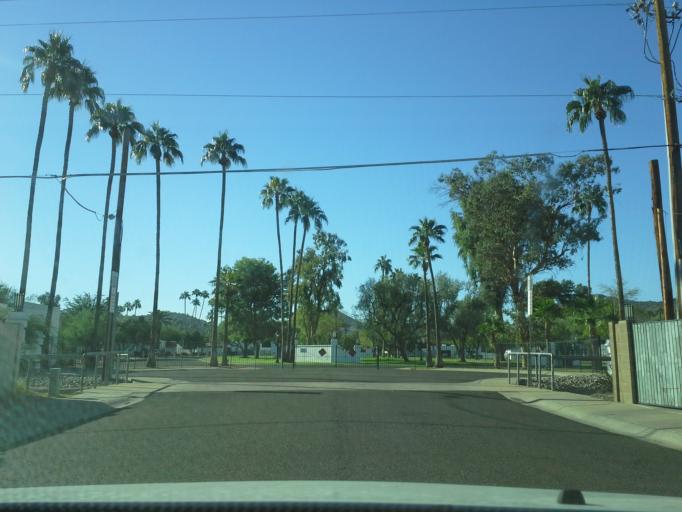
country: US
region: Arizona
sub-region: Maricopa County
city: Glendale
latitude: 33.6150
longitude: -112.0719
